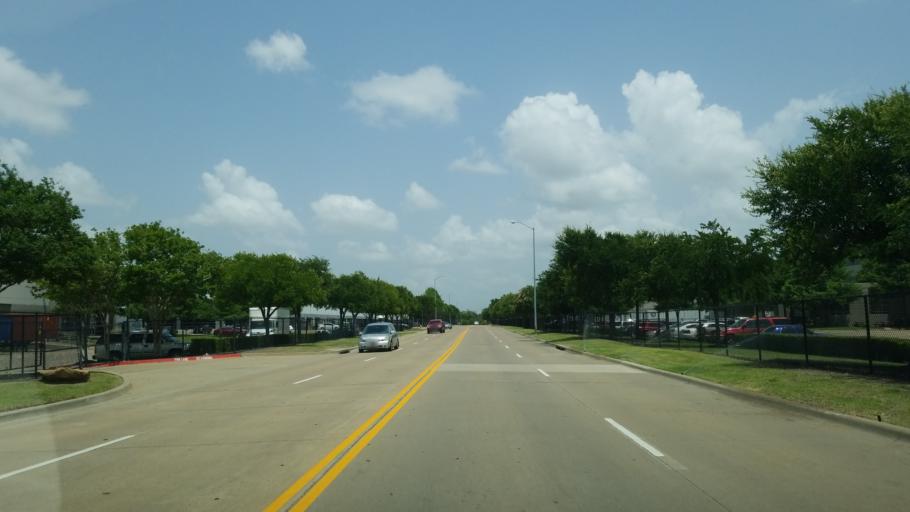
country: US
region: Texas
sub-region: Dallas County
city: Cockrell Hill
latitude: 32.7599
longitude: -96.8853
